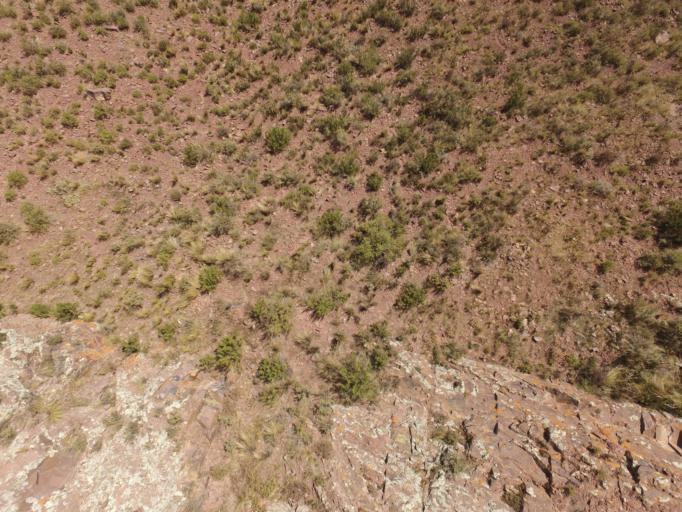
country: BO
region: Oruro
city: Challapata
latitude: -18.6924
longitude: -66.7551
